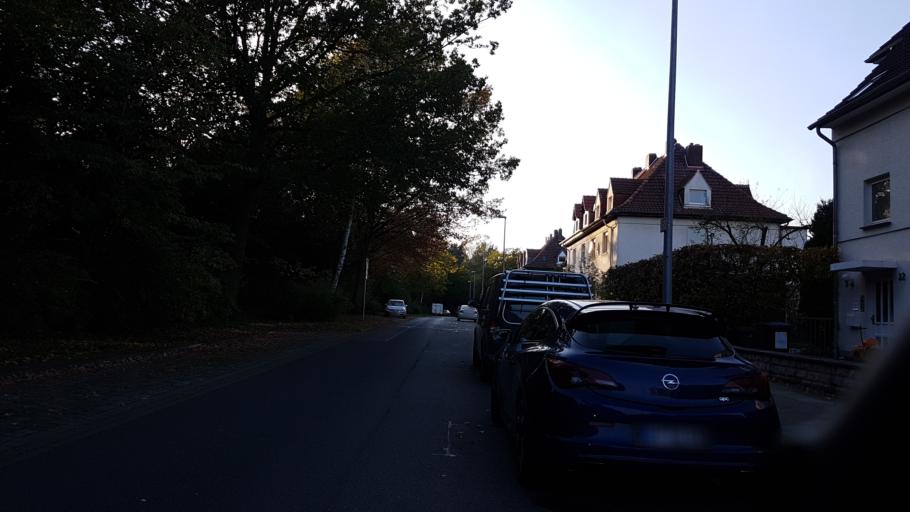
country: DE
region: Lower Saxony
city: Hemmingen
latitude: 52.3351
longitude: 9.7129
